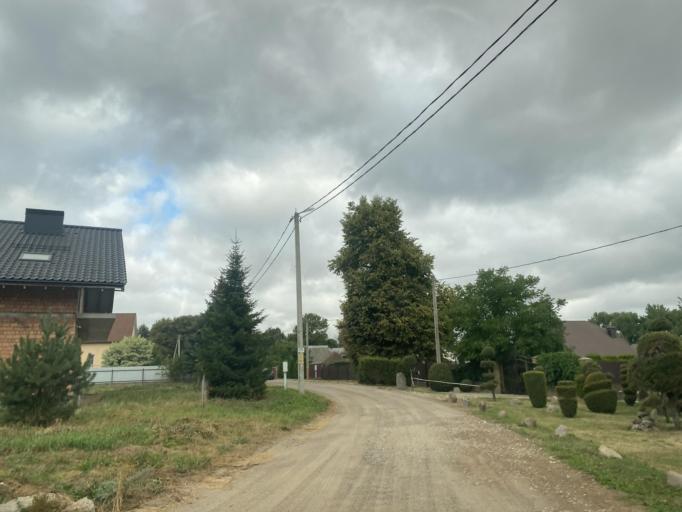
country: BY
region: Minsk
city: Bal'shavik
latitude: 53.9875
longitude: 27.5876
